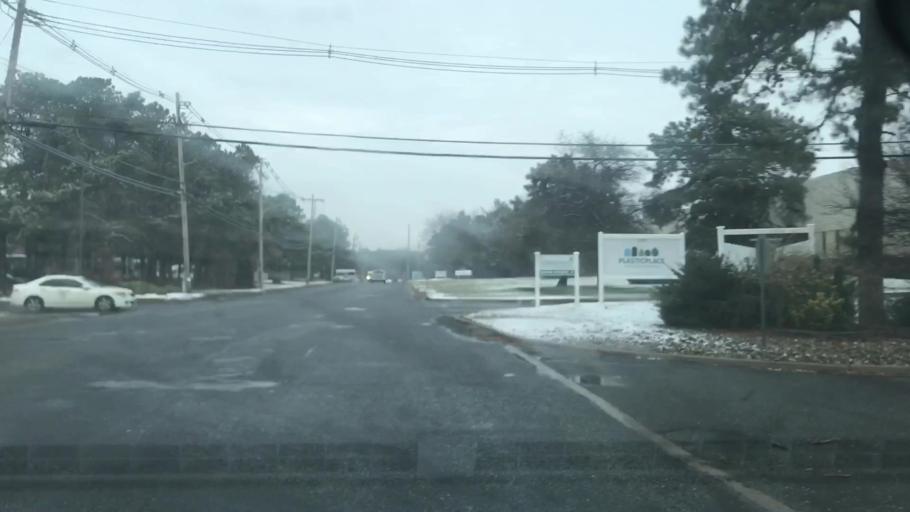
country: US
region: New Jersey
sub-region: Ocean County
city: Leisure Village
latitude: 40.0547
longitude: -74.1793
